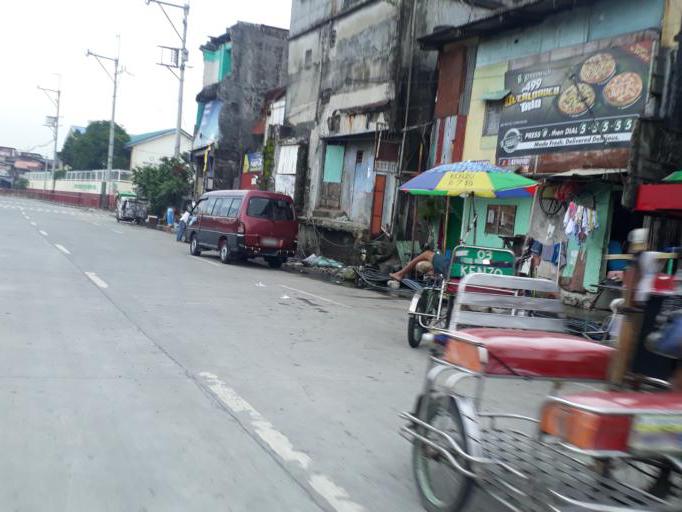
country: PH
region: Metro Manila
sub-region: Caloocan City
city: Niugan
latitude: 14.6472
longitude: 120.9506
